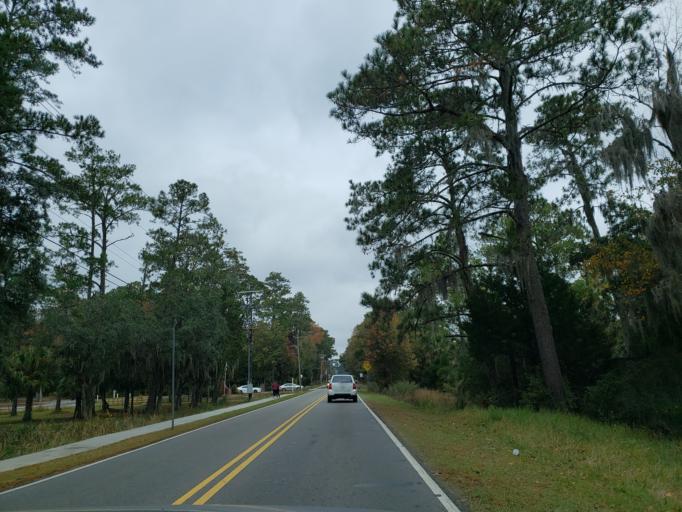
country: US
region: Georgia
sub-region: Chatham County
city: Wilmington Island
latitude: 32.0122
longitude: -80.9742
